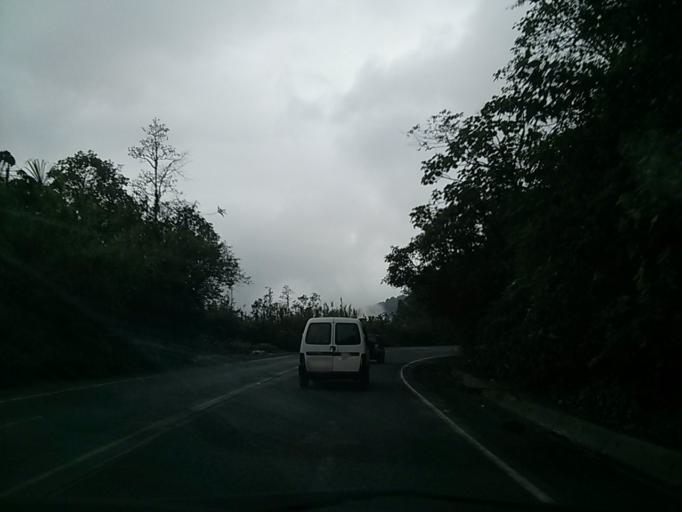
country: CR
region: San Jose
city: Dulce Nombre de Jesus
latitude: 10.0683
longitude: -83.9874
